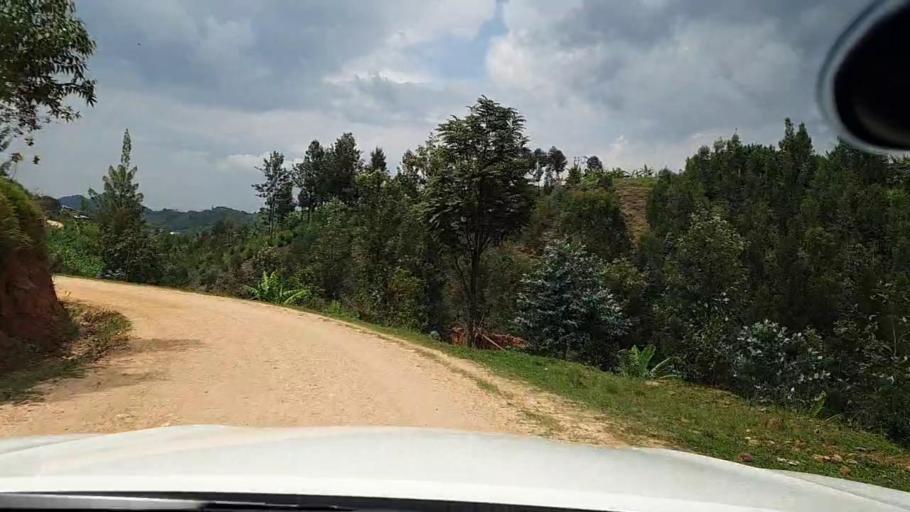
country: RW
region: Western Province
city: Kibuye
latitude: -2.1186
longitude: 29.4247
